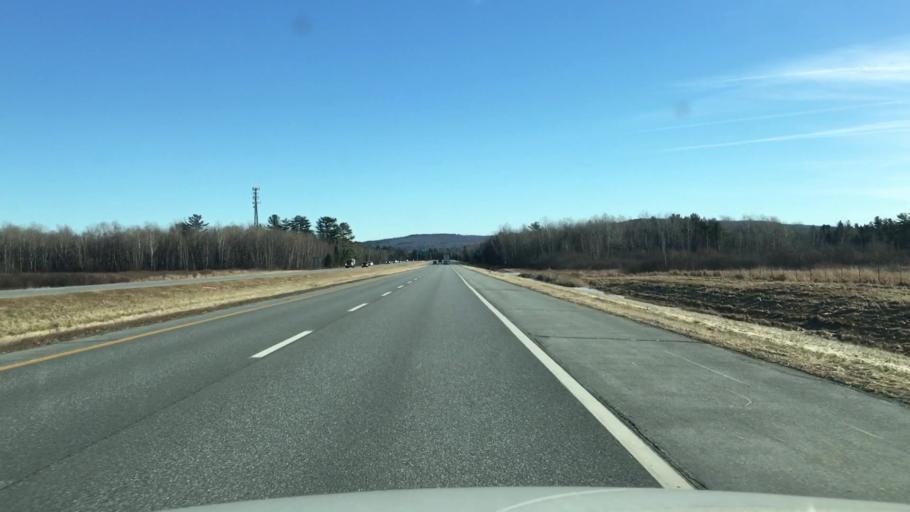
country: US
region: Maine
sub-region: Penobscot County
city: Brewer
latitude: 44.7731
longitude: -68.7448
